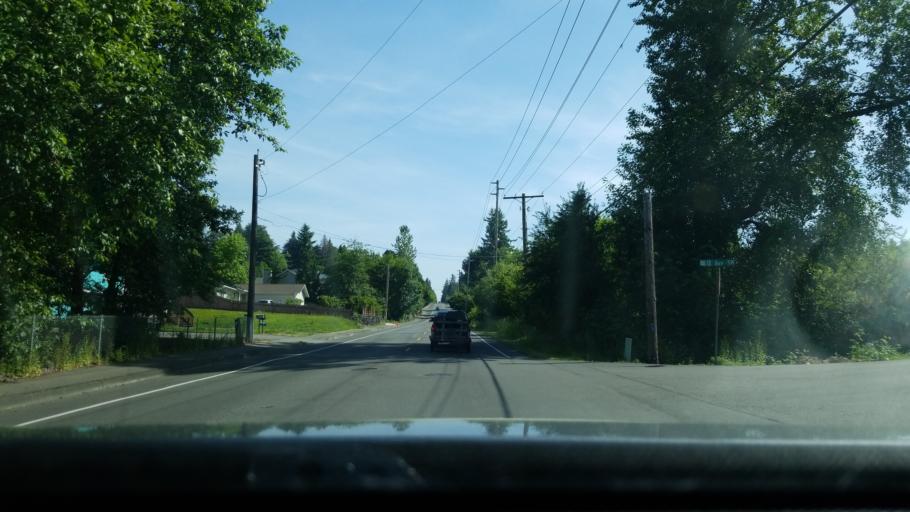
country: US
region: Washington
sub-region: Pierce County
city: Puyallup
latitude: 47.1747
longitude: -122.3042
